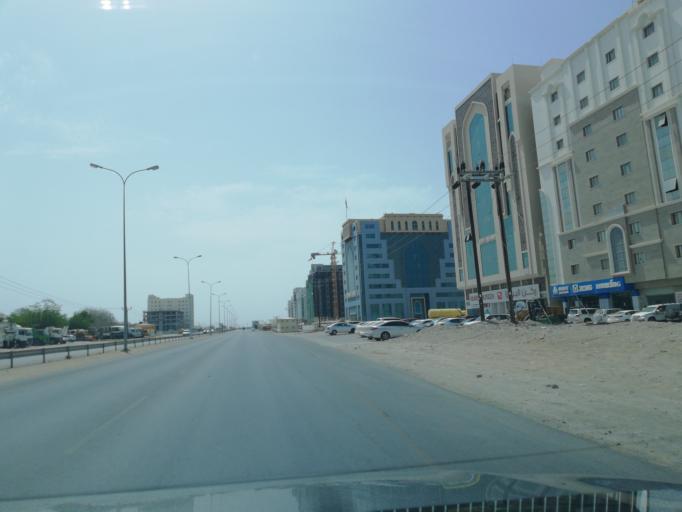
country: OM
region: Muhafazat Masqat
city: Bawshar
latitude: 23.5827
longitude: 58.3728
